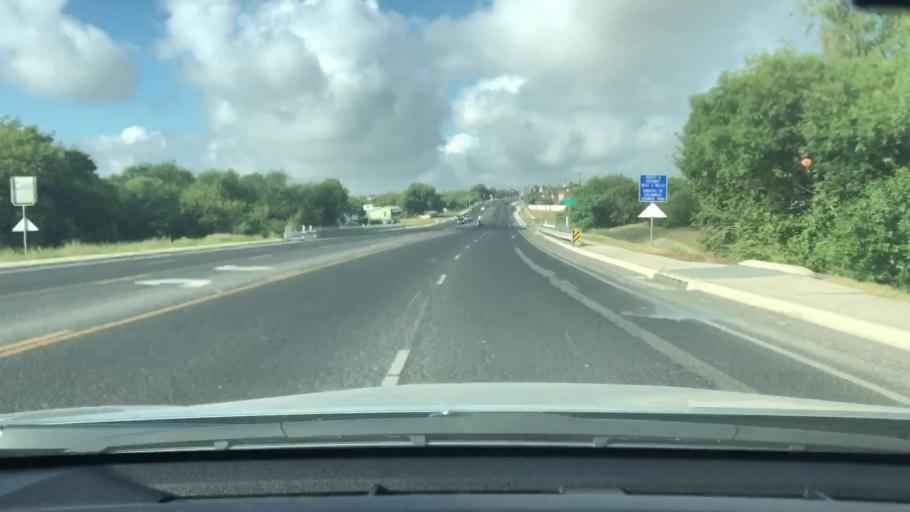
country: US
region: Texas
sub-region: Bexar County
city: Converse
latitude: 29.5057
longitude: -98.3093
